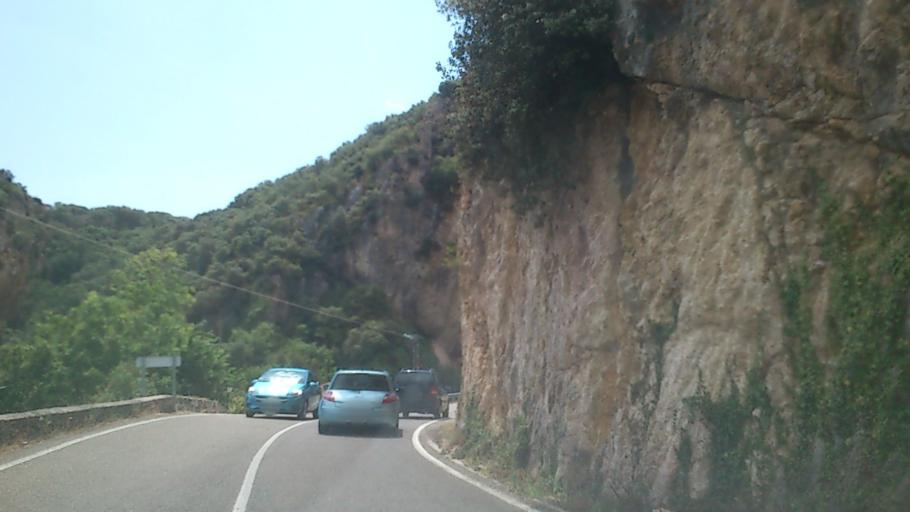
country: ES
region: Castille and Leon
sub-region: Provincia de Burgos
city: Frias
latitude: 42.7497
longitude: -3.3063
